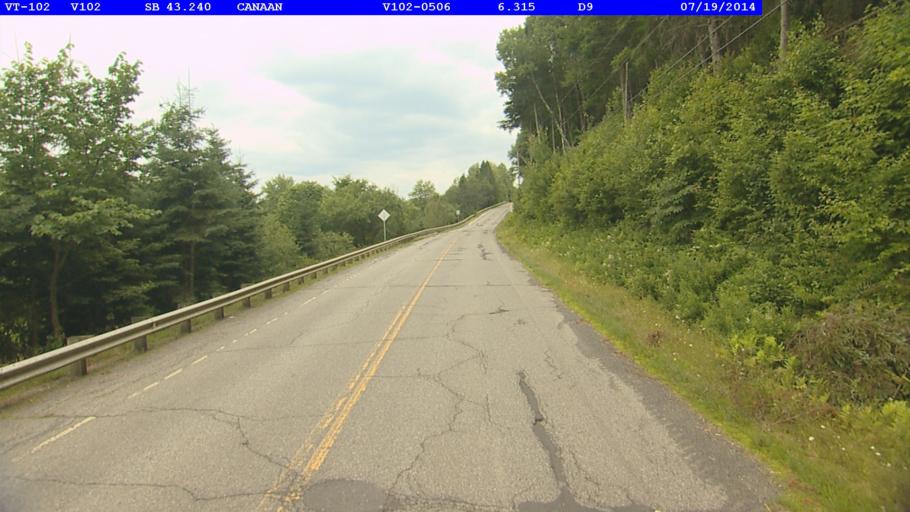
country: US
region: New Hampshire
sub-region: Coos County
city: Colebrook
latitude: 44.9896
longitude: -71.5424
